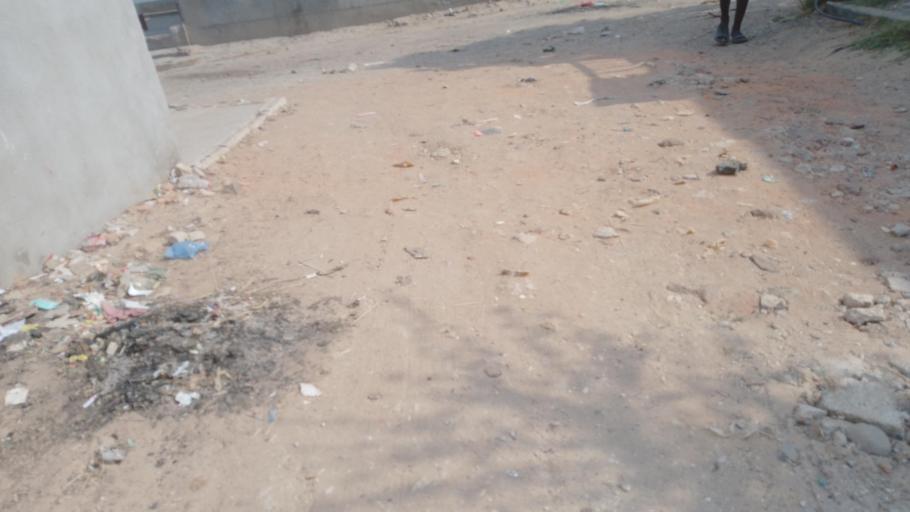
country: ZM
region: Lusaka
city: Lusaka
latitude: -15.4065
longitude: 28.3728
